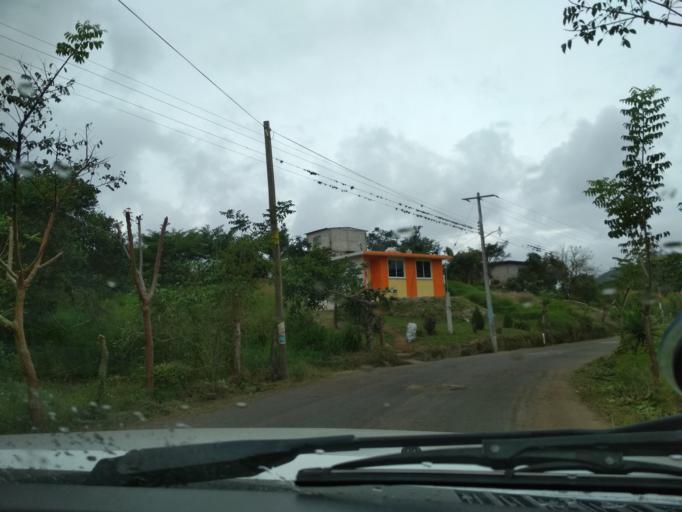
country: MX
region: Veracruz
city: El Castillo
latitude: 19.5355
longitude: -96.8168
